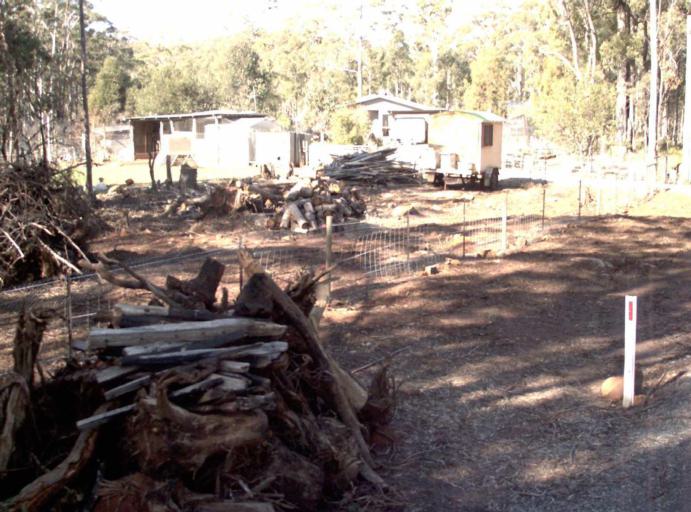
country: AU
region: Tasmania
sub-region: Launceston
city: Mayfield
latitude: -41.3177
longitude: 147.2083
